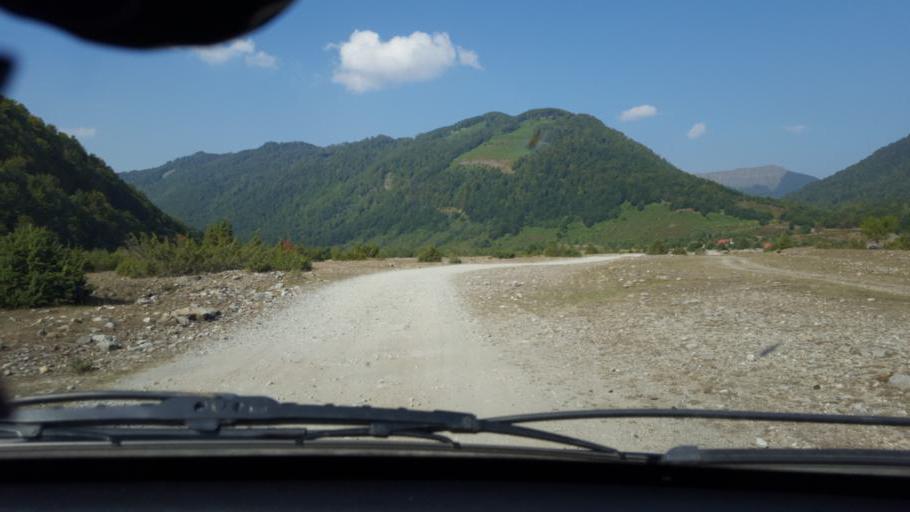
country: ME
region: Andrijevica
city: Andrijevica
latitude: 42.5974
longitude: 19.6656
